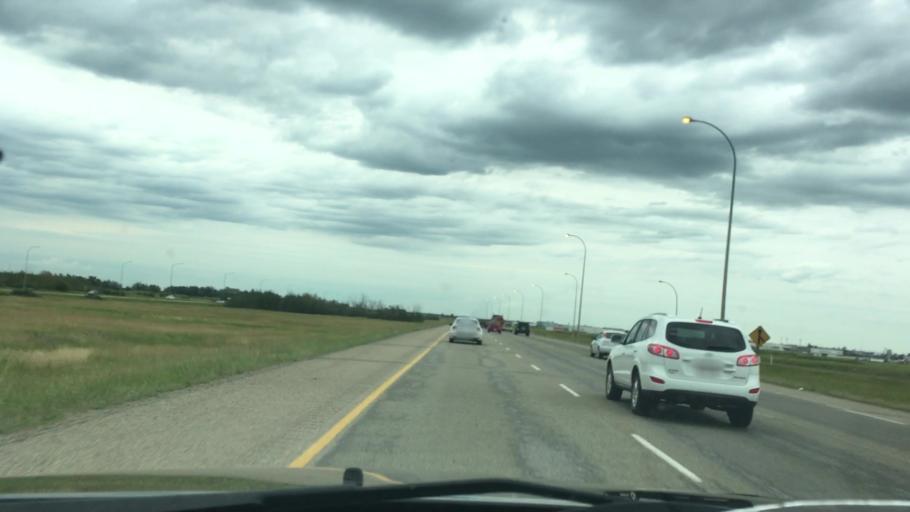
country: CA
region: Alberta
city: Leduc
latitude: 53.3125
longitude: -113.5480
